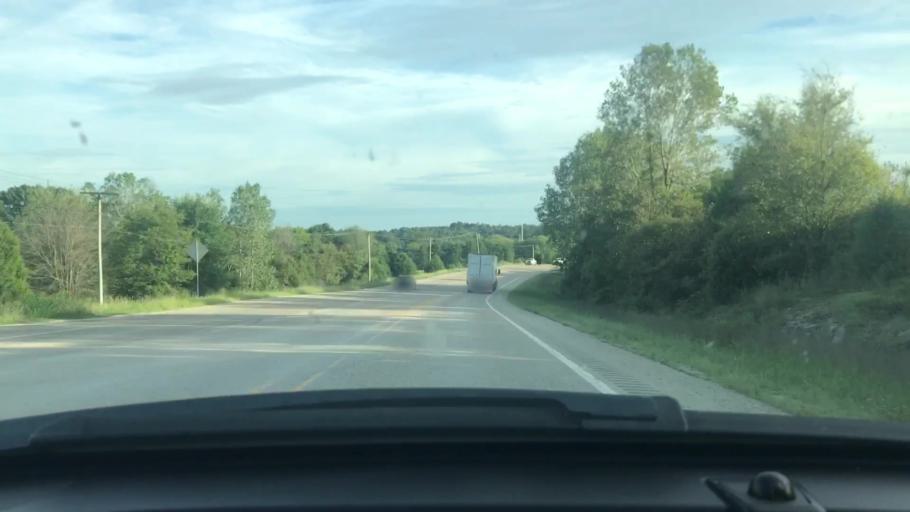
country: US
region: Arkansas
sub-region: Lawrence County
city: Hoxie
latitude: 36.1442
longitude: -91.1586
